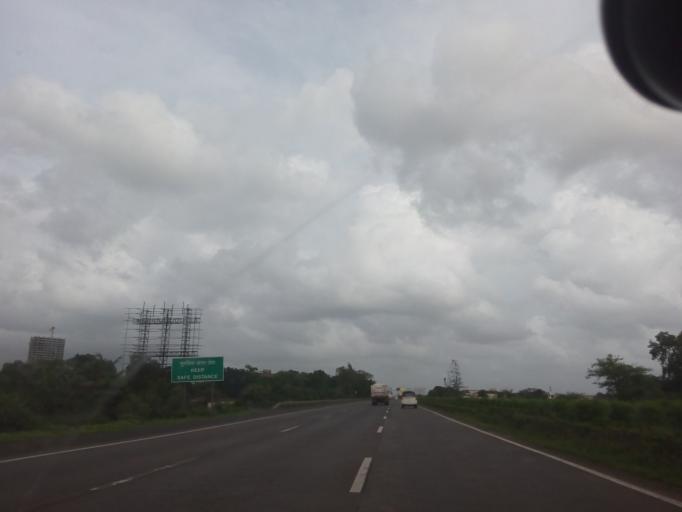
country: IN
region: Maharashtra
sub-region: Raigarh
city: Panvel
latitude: 19.0042
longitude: 73.1263
